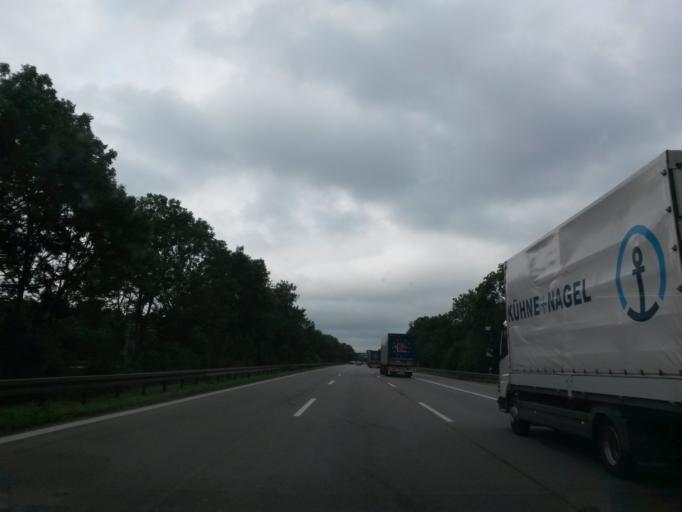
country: DE
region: Bavaria
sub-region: Upper Bavaria
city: Vaterstetten
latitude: 48.1235
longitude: 11.7586
